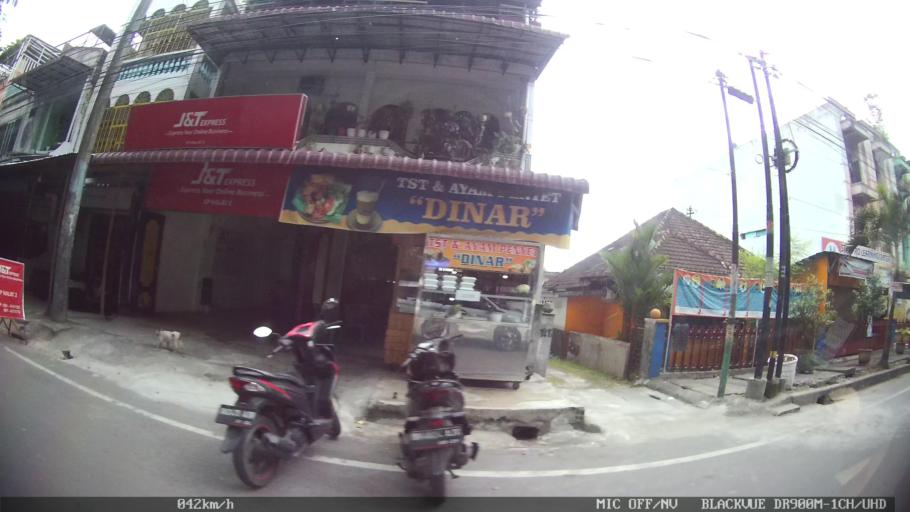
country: ID
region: North Sumatra
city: Medan
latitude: 3.5724
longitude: 98.6940
